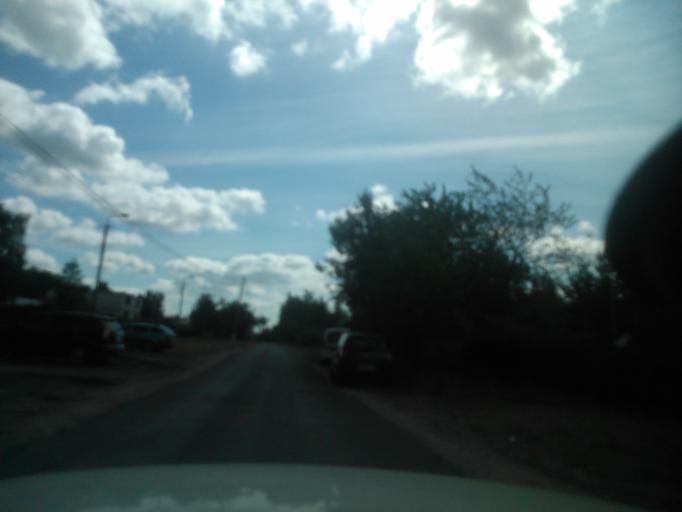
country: PL
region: Kujawsko-Pomorskie
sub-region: Powiat torunski
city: Lubicz Gorny
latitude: 53.0223
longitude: 18.7812
